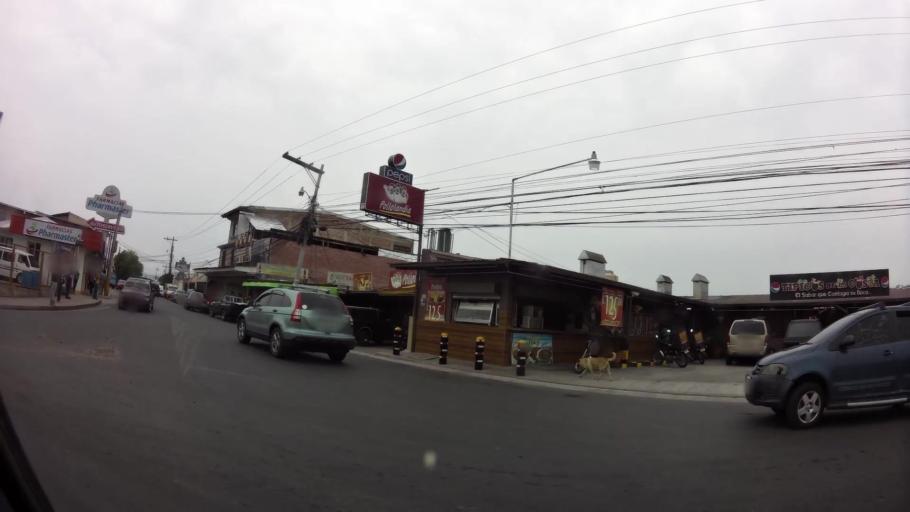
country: HN
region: Francisco Morazan
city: Yaguacire
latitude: 14.0428
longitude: -87.2228
